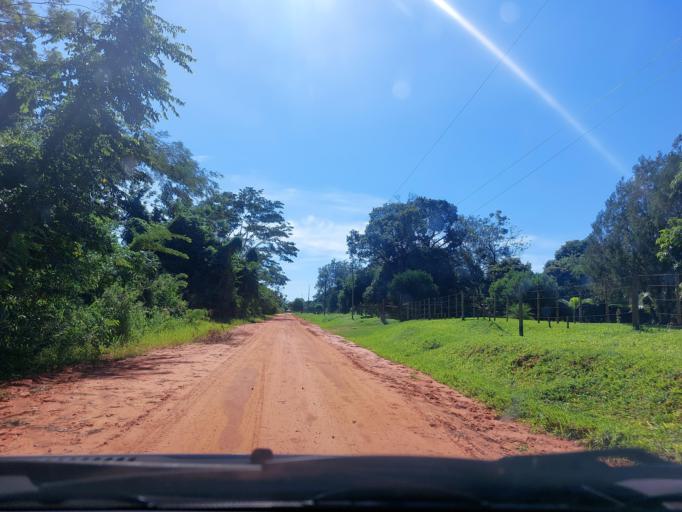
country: PY
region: San Pedro
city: Itacurubi del Rosario
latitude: -24.5382
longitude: -56.5802
